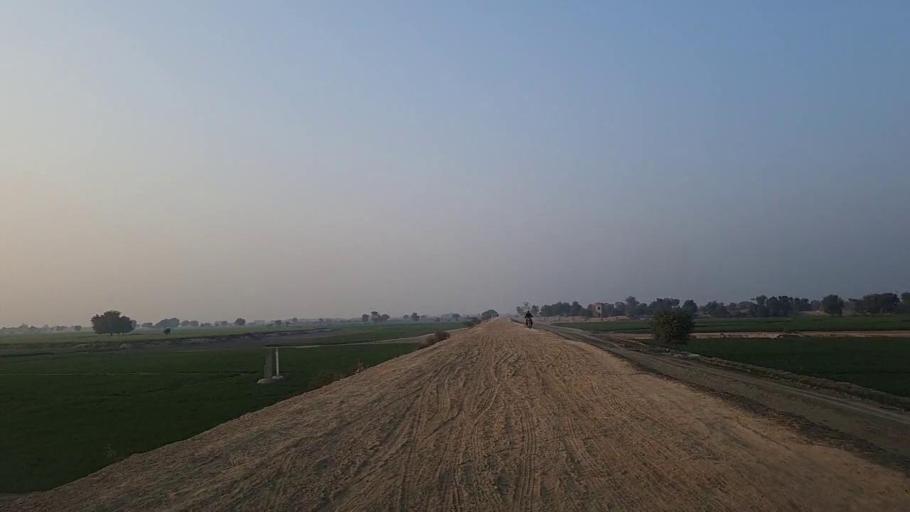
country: PK
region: Sindh
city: Sann
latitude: 26.1900
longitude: 68.0910
